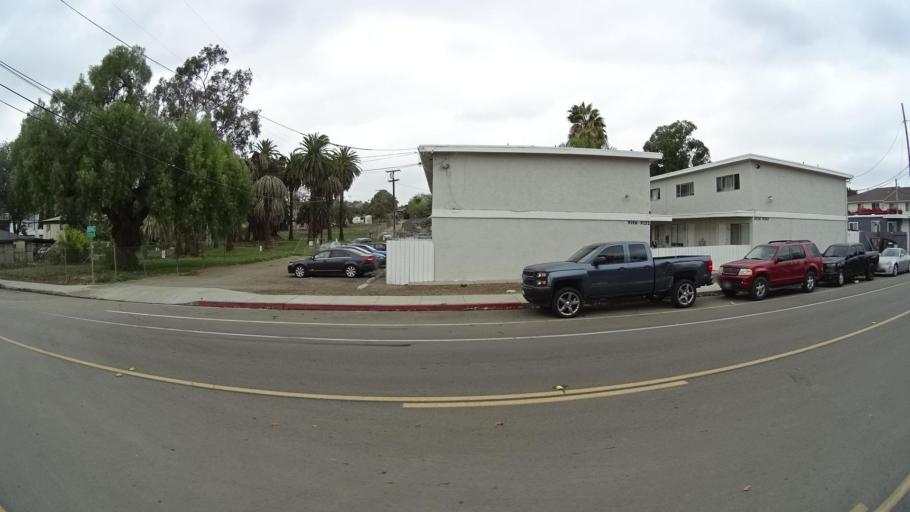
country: US
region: California
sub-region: San Diego County
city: Spring Valley
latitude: 32.7446
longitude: -117.0006
